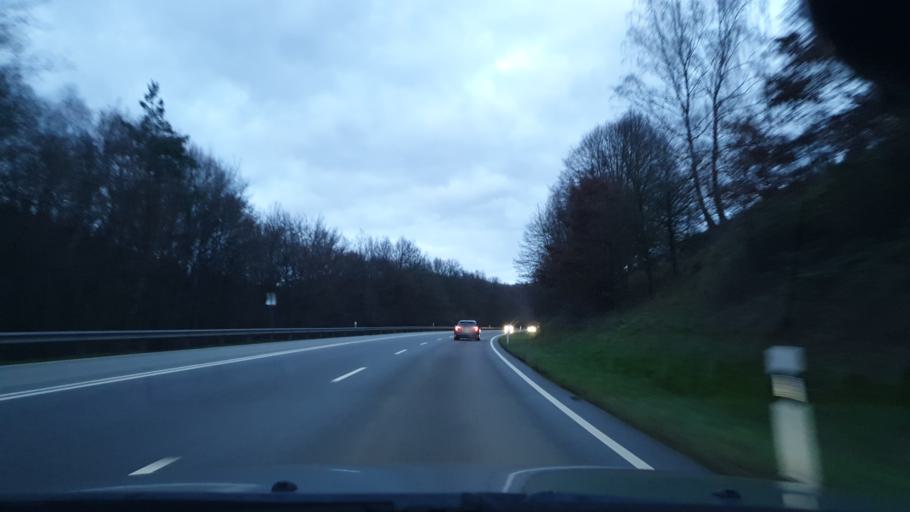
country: DE
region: Rheinland-Pfalz
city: Steinalben
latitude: 49.3057
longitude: 7.6628
